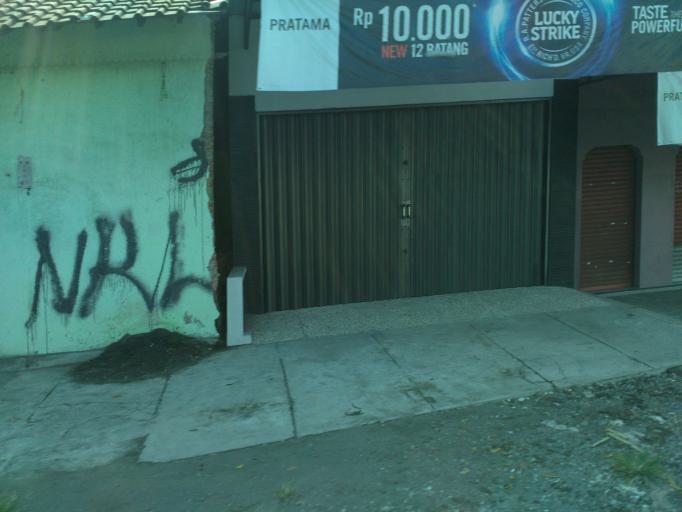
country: ID
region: Central Java
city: Delanggu
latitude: -7.6310
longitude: 110.6941
